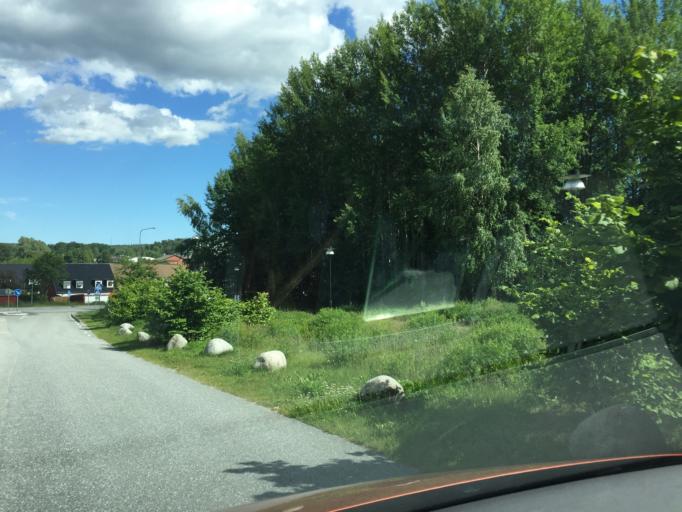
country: SE
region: Stockholm
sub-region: Botkyrka Kommun
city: Tumba
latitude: 59.2036
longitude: 17.8232
